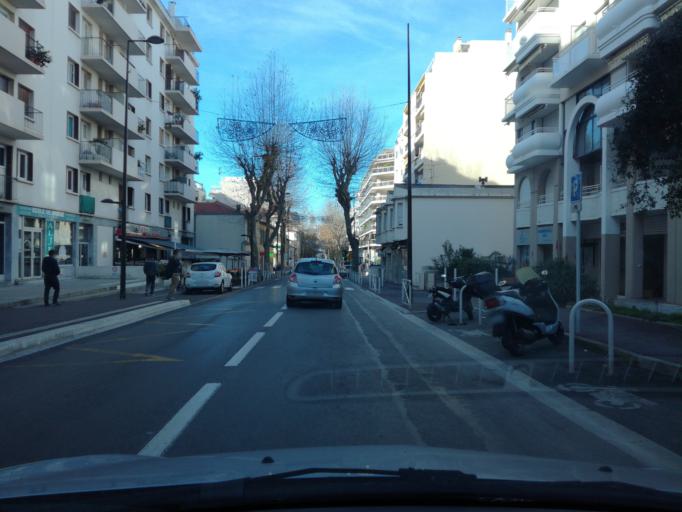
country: FR
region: Provence-Alpes-Cote d'Azur
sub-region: Departement des Alpes-Maritimes
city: Antibes
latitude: 43.5716
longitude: 7.1102
